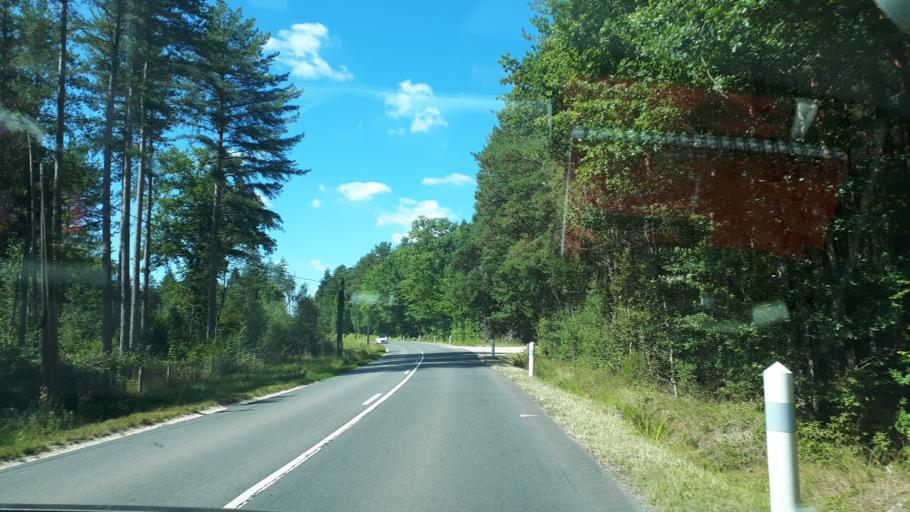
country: FR
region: Centre
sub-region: Departement du Loir-et-Cher
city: Lamotte-Beuvron
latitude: 47.5883
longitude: 1.9974
